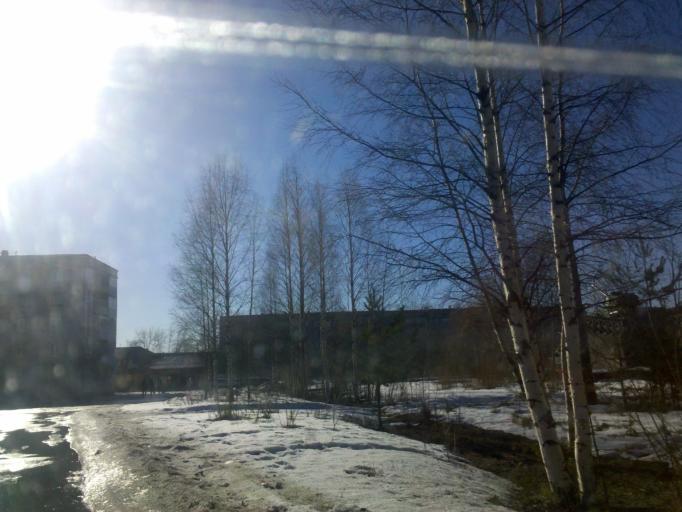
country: RU
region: Republic of Karelia
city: Medvezh'yegorsk
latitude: 62.9151
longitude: 34.4754
